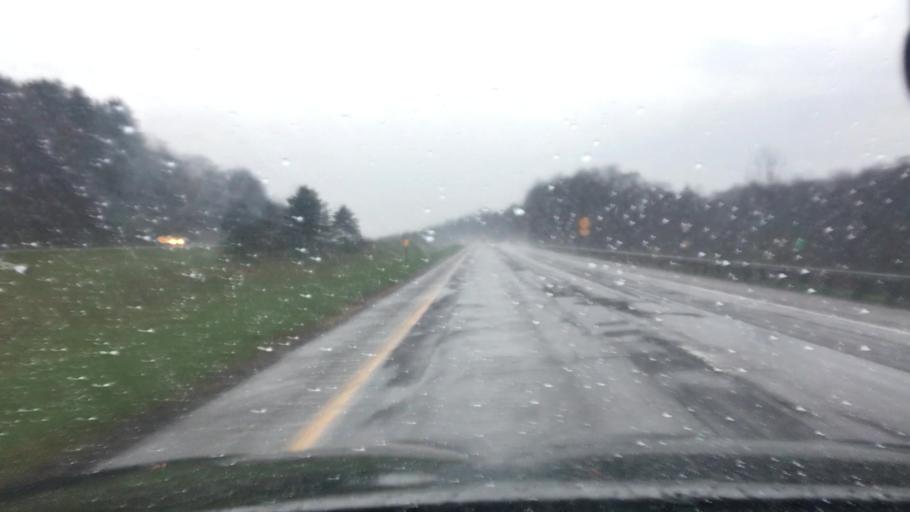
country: US
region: New York
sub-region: Chautauqua County
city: Lakewood
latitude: 42.1326
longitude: -79.3286
